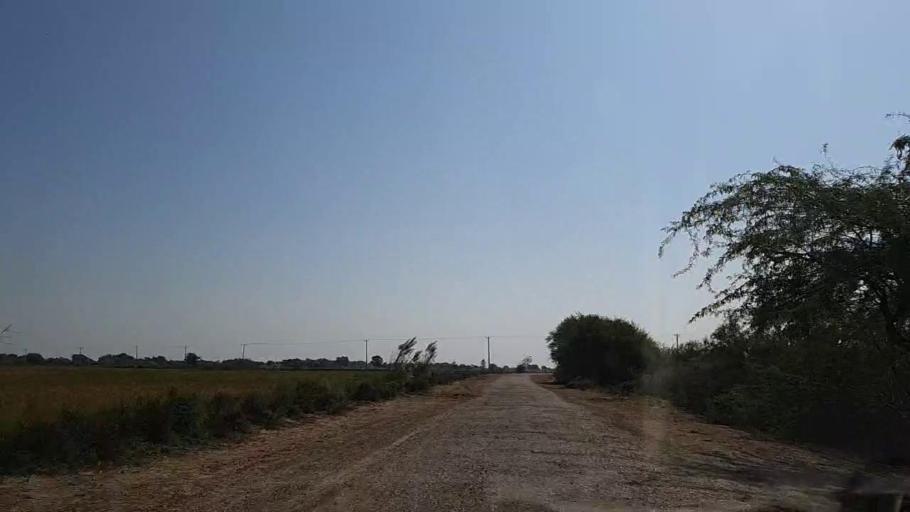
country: PK
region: Sindh
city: Chuhar Jamali
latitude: 24.5224
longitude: 68.0921
